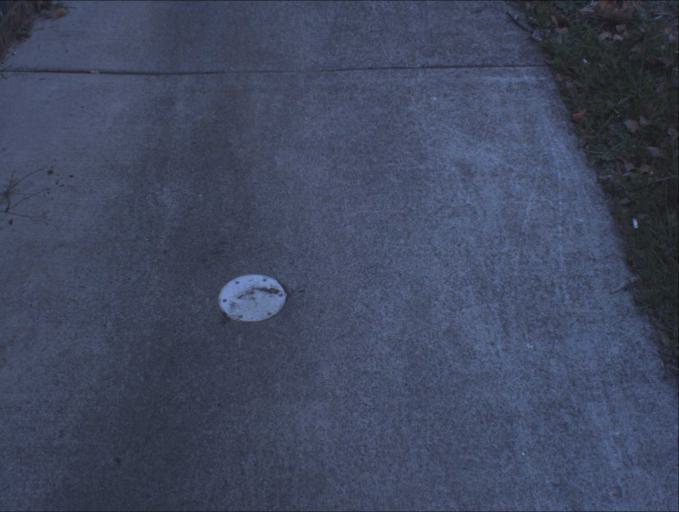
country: AU
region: Queensland
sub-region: Logan
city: Springwood
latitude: -27.5985
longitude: 153.1475
